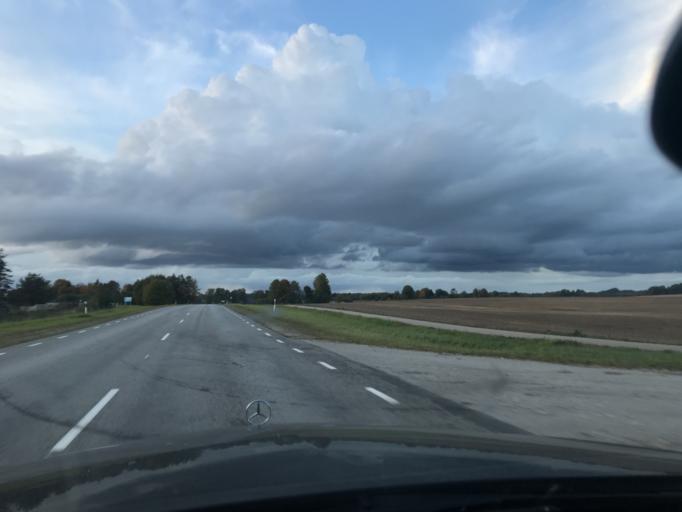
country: EE
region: Vorumaa
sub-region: Antsla vald
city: Vana-Antsla
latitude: 57.9329
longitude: 26.3165
